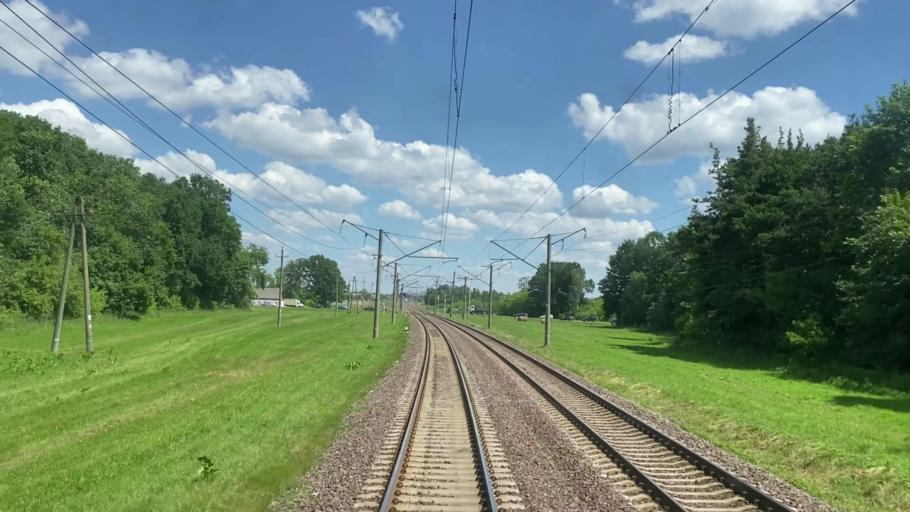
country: BY
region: Brest
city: Ivatsevichy
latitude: 52.6954
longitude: 25.3125
